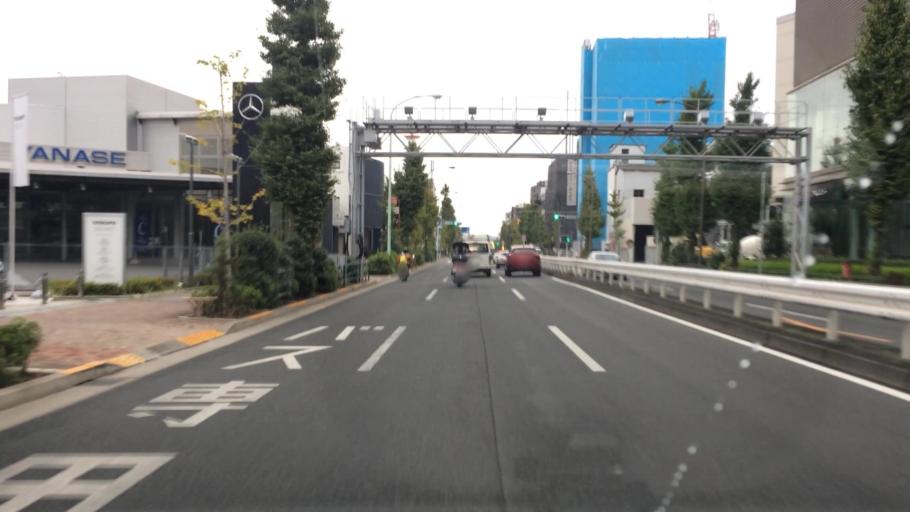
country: JP
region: Tokyo
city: Tokyo
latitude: 35.6236
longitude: 139.6856
